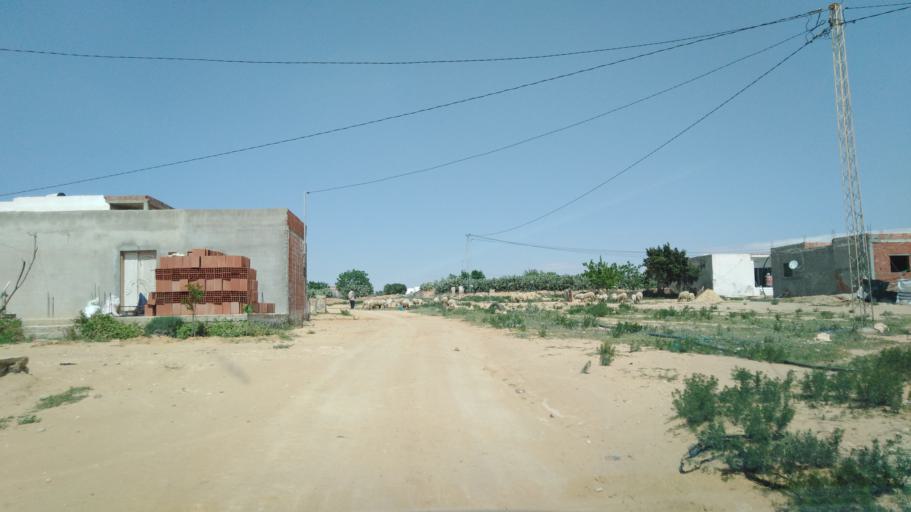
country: TN
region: Safaqis
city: Sfax
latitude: 34.7633
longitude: 10.5214
